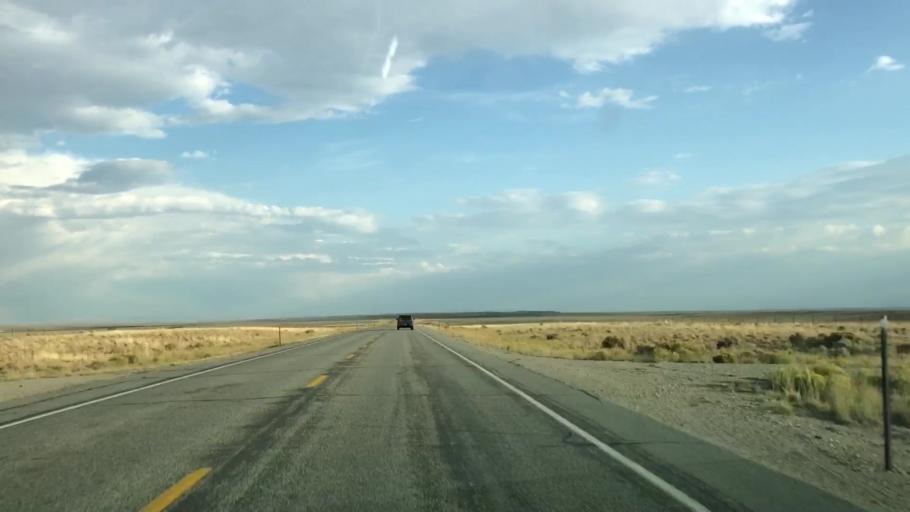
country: US
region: Wyoming
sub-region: Sublette County
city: Marbleton
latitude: 42.3351
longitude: -109.5191
